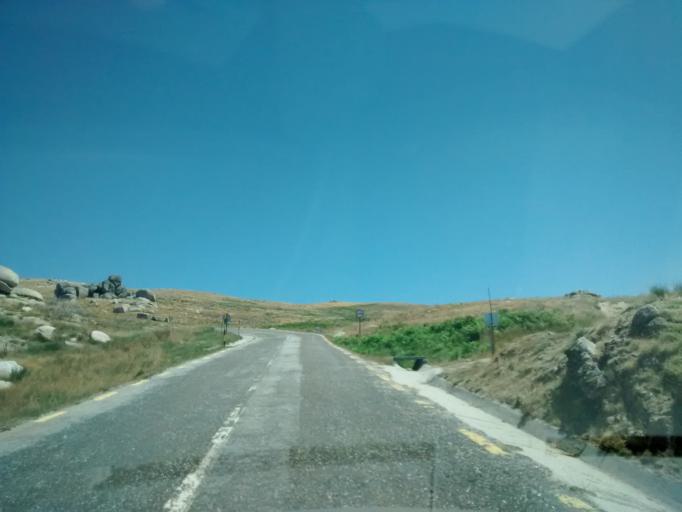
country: PT
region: Guarda
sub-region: Seia
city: Seia
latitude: 40.4154
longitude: -7.6382
